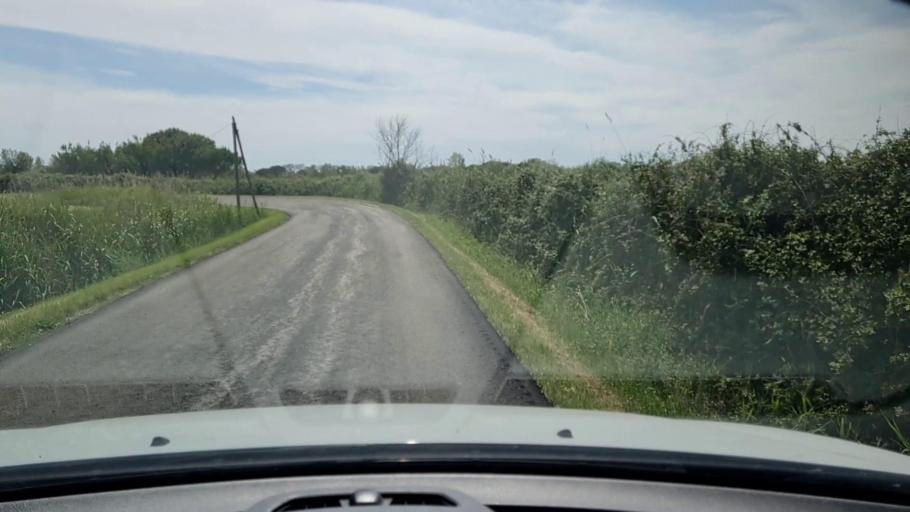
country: FR
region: Languedoc-Roussillon
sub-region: Departement du Gard
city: Saint-Gilles
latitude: 43.5708
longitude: 4.3943
